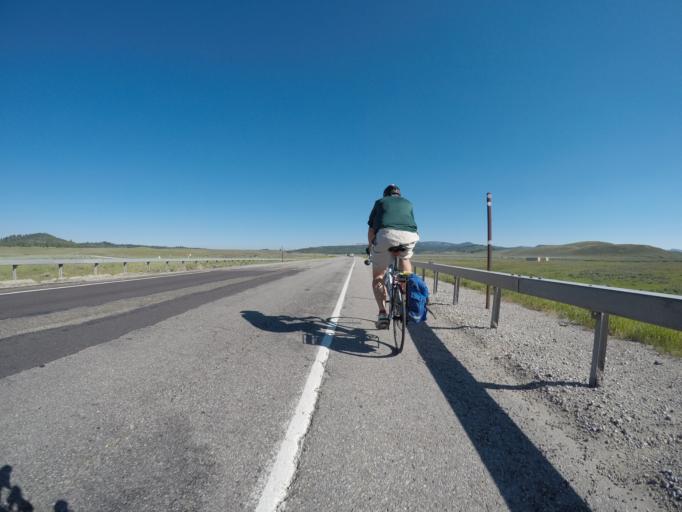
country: US
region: Wyoming
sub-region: Sublette County
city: Pinedale
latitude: 43.1116
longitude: -110.1740
